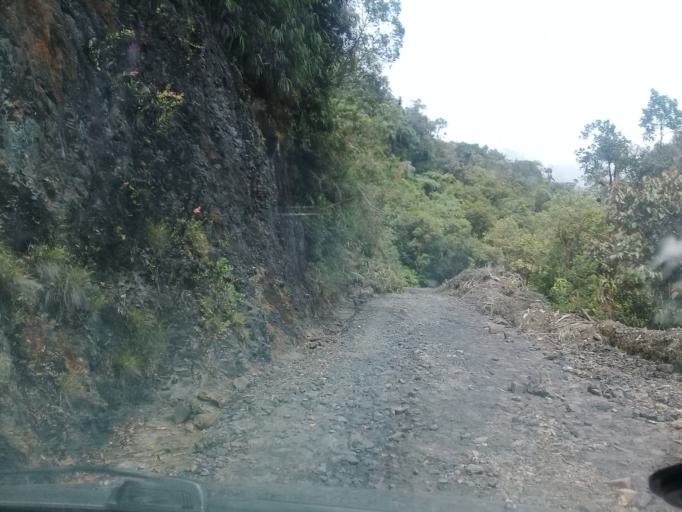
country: CO
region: Cundinamarca
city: Gachala
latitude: 4.6986
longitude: -73.4166
